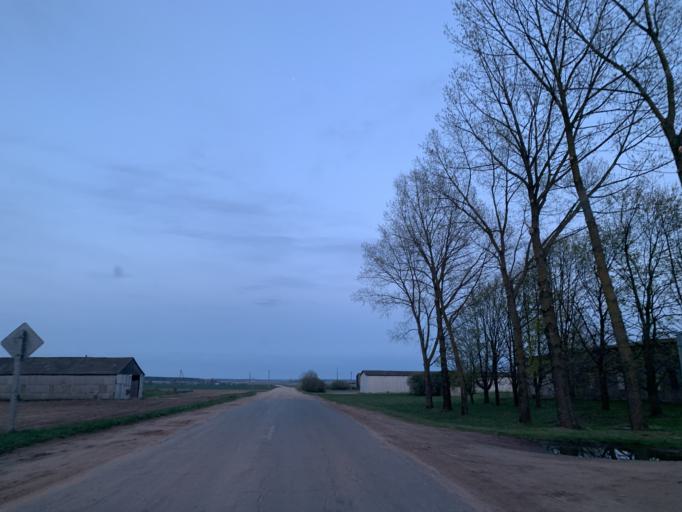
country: BY
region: Minsk
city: Snow
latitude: 53.1662
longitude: 26.5201
